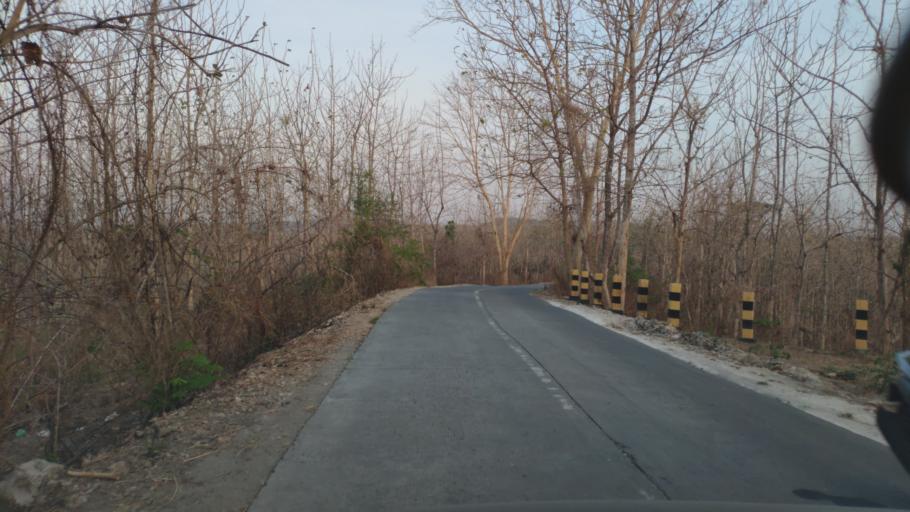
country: ID
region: Central Java
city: Klopoduwur
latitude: -7.0503
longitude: 111.4058
